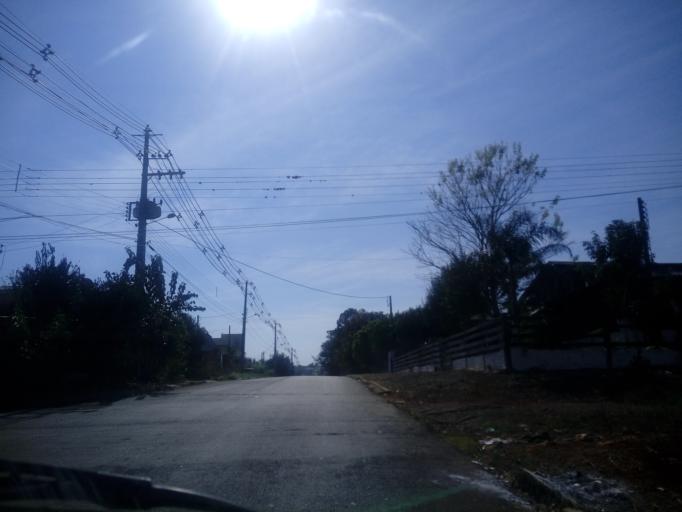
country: BR
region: Santa Catarina
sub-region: Chapeco
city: Chapeco
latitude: -27.0824
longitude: -52.6414
